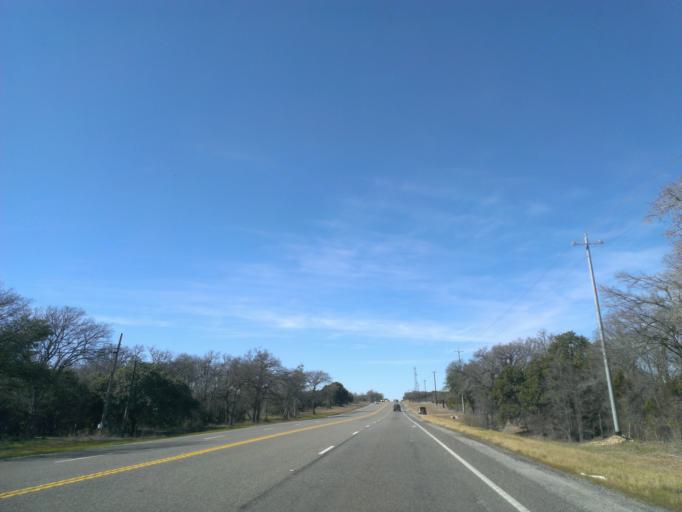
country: US
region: Texas
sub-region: Burnet County
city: Marble Falls
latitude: 30.4751
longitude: -98.1855
